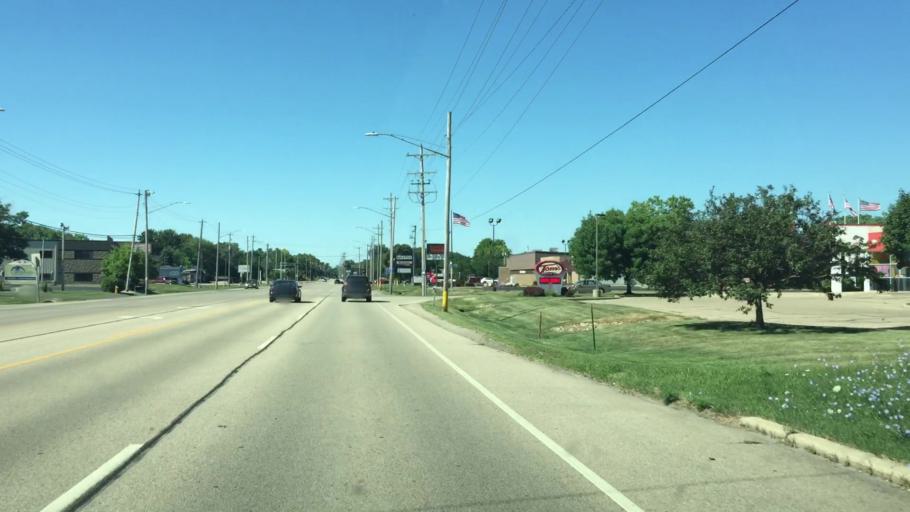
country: US
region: Wisconsin
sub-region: Winnebago County
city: Menasha
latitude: 44.2247
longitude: -88.4257
